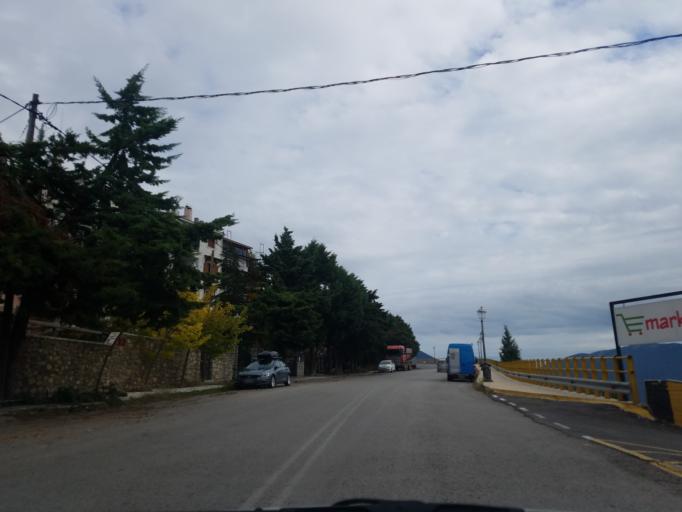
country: GR
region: Central Greece
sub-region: Nomos Voiotias
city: Arachova
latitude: 38.4802
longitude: 22.5781
